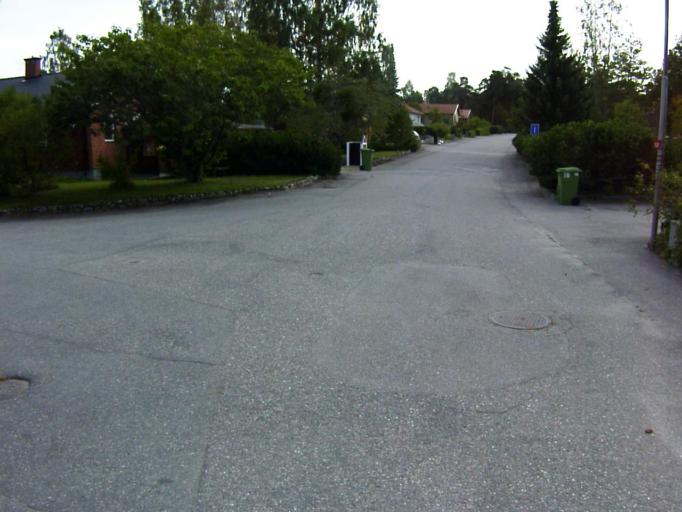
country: SE
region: Soedermanland
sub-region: Eskilstuna Kommun
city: Arla
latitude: 59.3890
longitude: 16.6744
